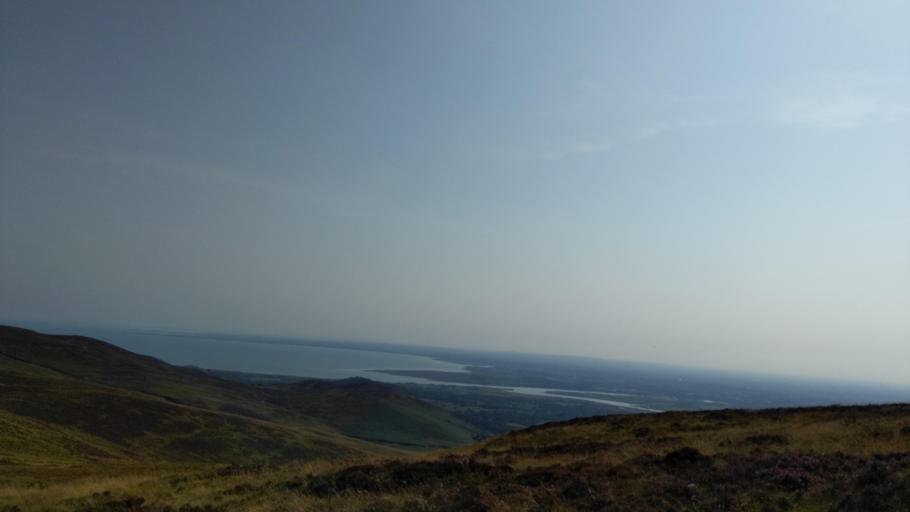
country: GB
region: Northern Ireland
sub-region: Down District
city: Warrenpoint
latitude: 54.0778
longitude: -6.3176
